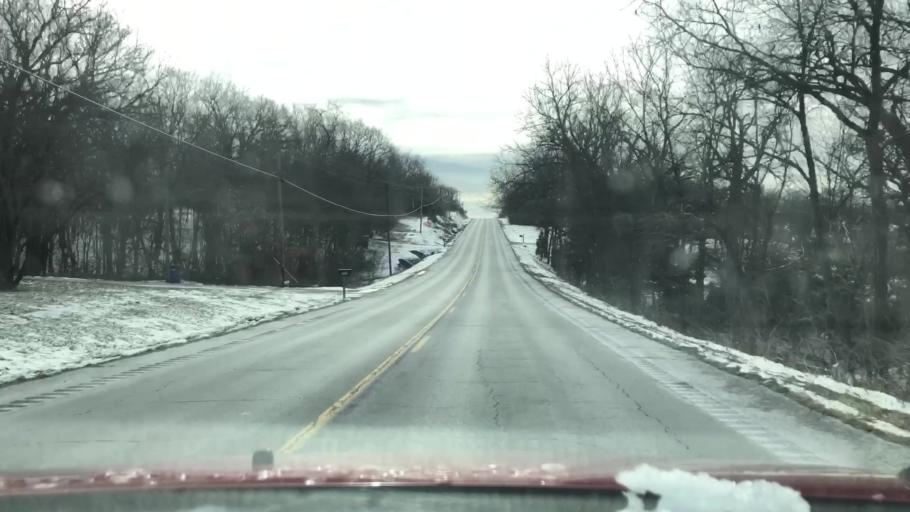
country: US
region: Missouri
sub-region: Jackson County
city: Oak Grove
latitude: 38.9720
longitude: -94.1307
